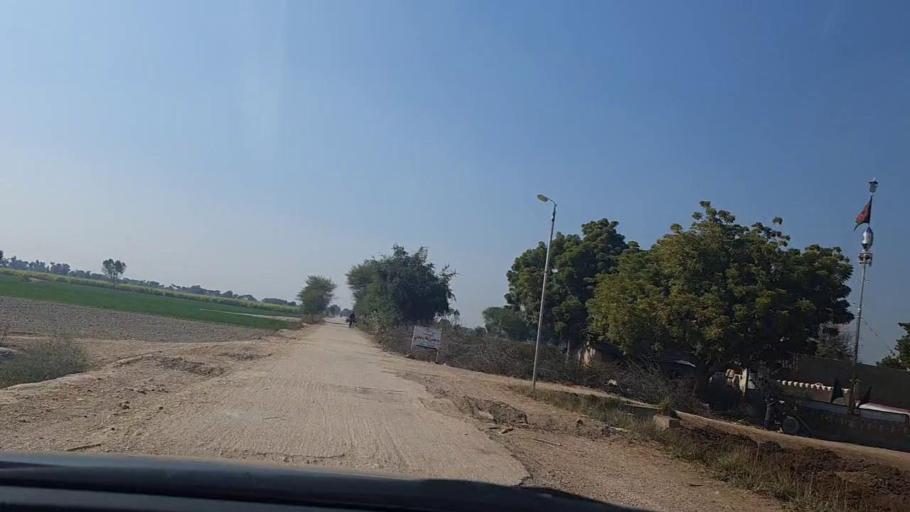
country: PK
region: Sindh
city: Daulatpur
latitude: 26.2844
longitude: 68.0588
